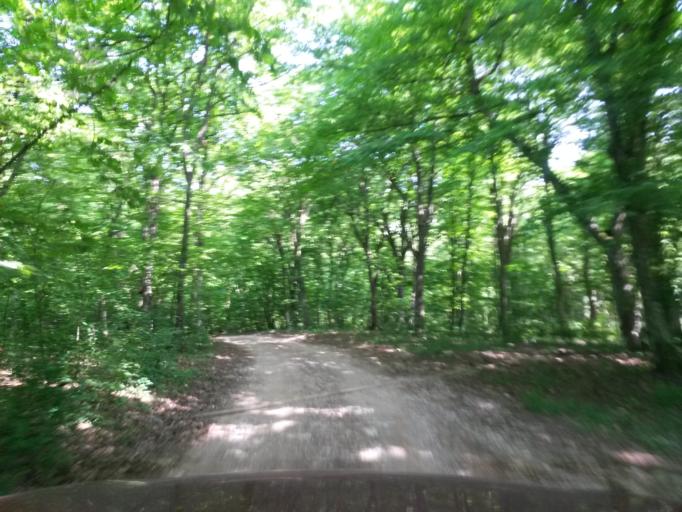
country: SK
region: Kosicky
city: Moldava nad Bodvou
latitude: 48.6423
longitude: 20.9552
